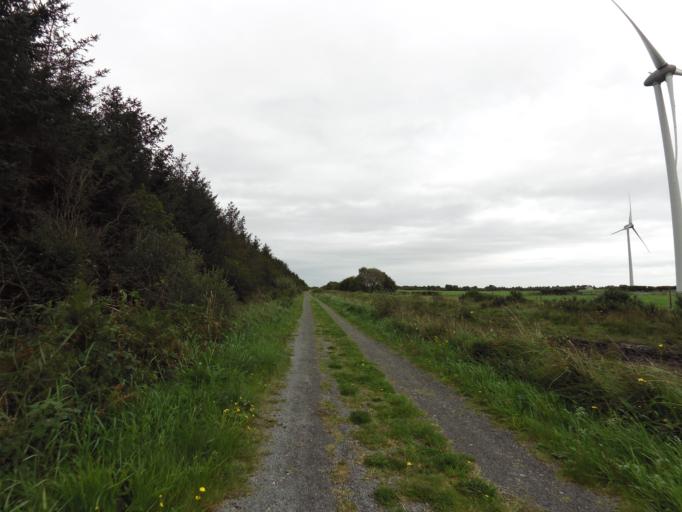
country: IE
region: Leinster
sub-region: Uibh Fhaili
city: Ferbane
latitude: 53.2328
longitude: -7.7714
